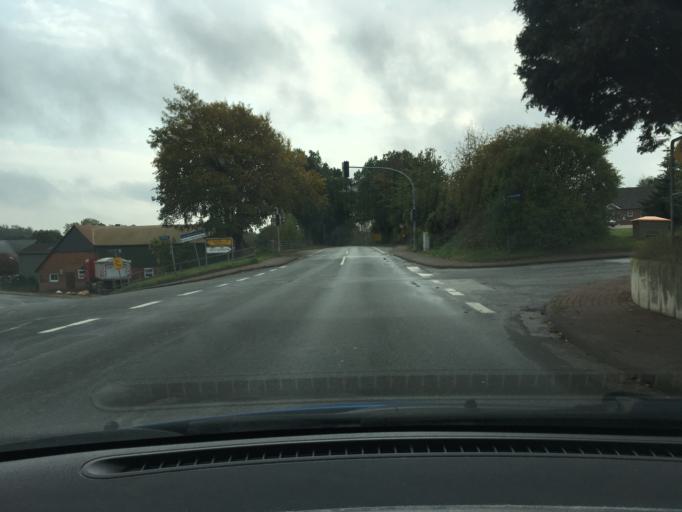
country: DE
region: Schleswig-Holstein
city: Tensfeld
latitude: 54.0433
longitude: 10.3181
